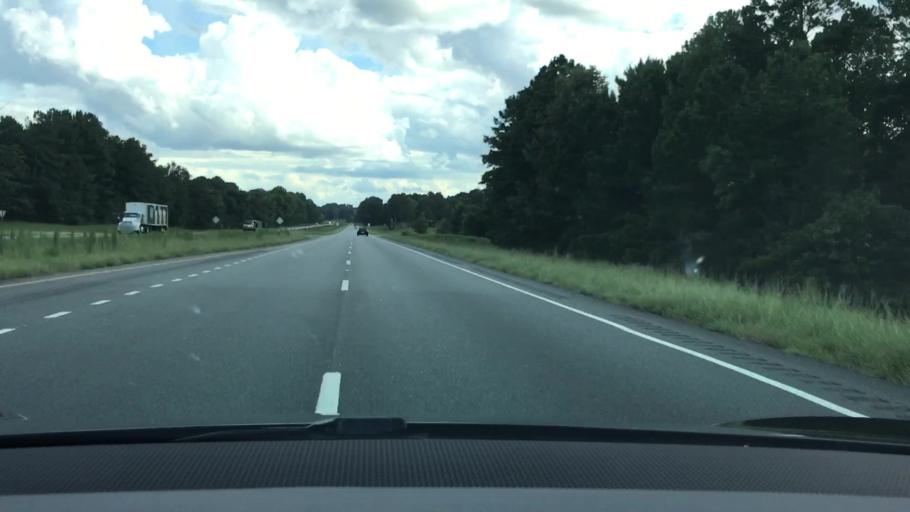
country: US
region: Alabama
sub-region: Pike County
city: Troy
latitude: 31.9591
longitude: -86.0254
